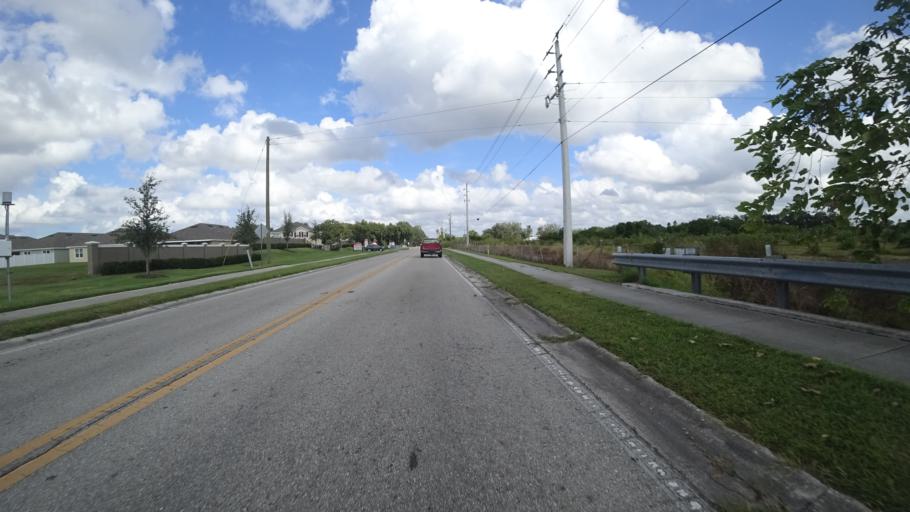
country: US
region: Florida
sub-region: Manatee County
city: Samoset
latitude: 27.4792
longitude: -82.5302
